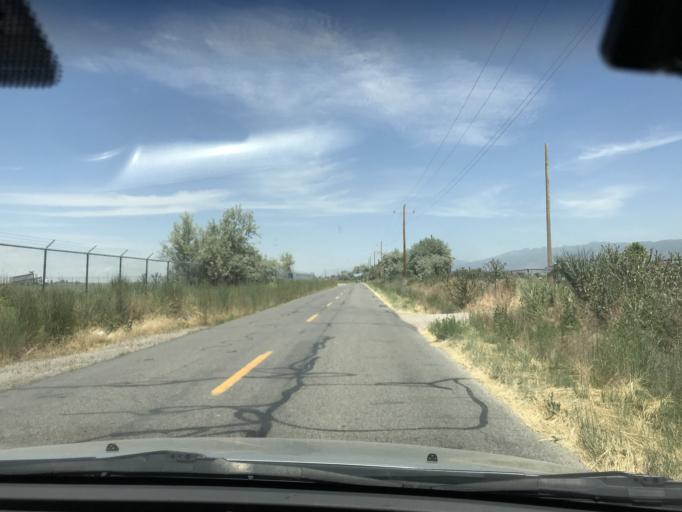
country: US
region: Utah
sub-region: Davis County
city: North Salt Lake
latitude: 40.8210
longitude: -111.9535
